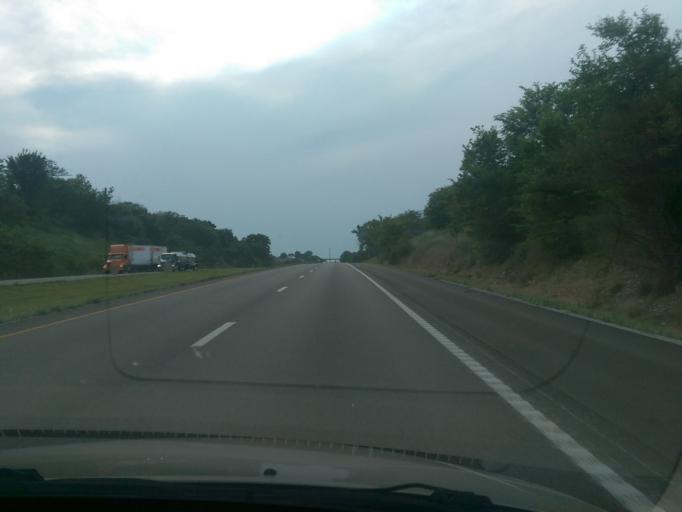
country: US
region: Missouri
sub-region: Andrew County
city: Savannah
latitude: 39.9078
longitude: -94.8910
